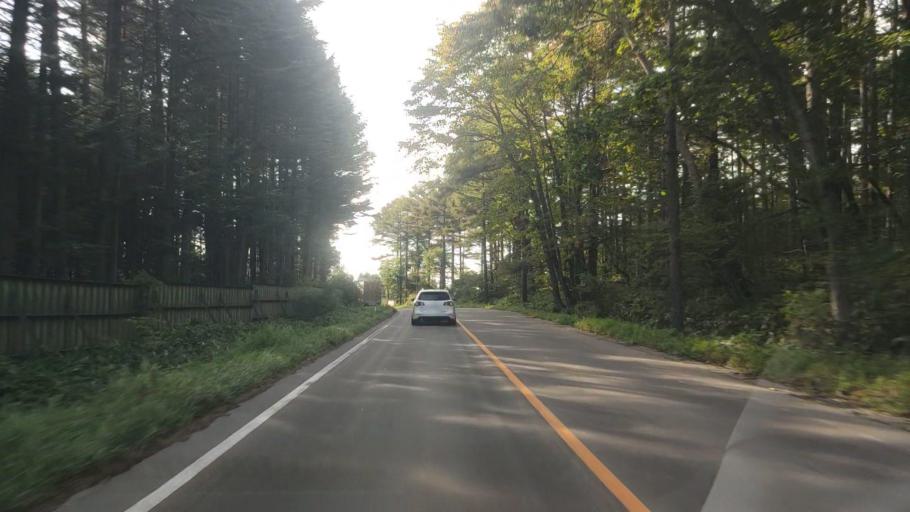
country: JP
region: Nagano
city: Ueda
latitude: 36.4900
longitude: 138.3983
